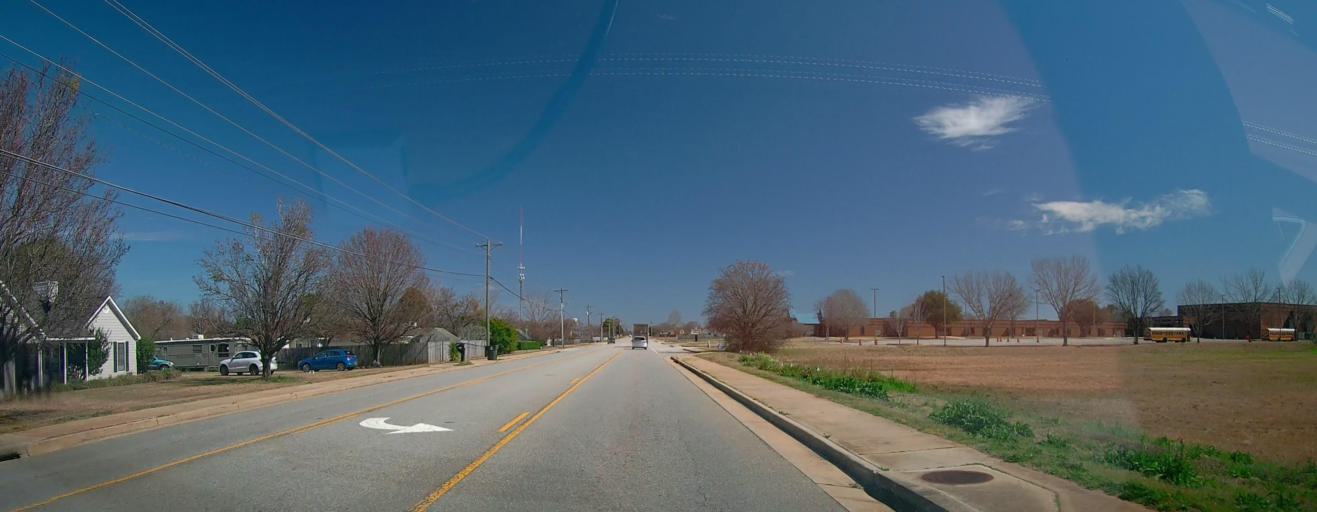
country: US
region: Georgia
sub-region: Houston County
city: Centerville
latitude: 32.5709
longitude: -83.6788
